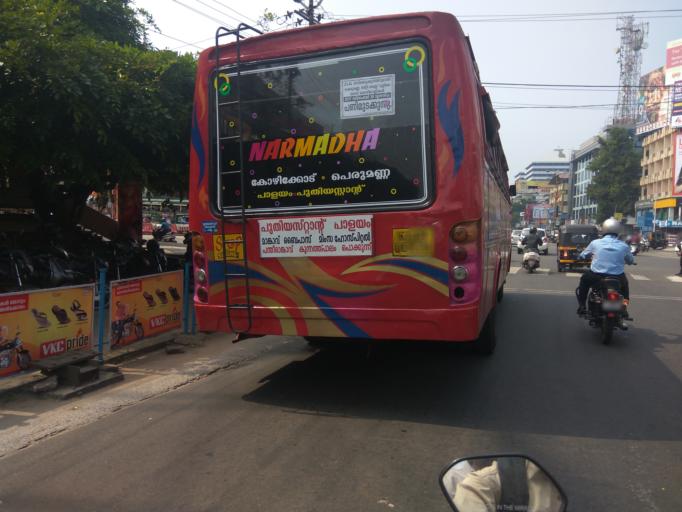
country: IN
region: Kerala
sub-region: Kozhikode
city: Kozhikode
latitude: 11.2594
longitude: 75.7862
